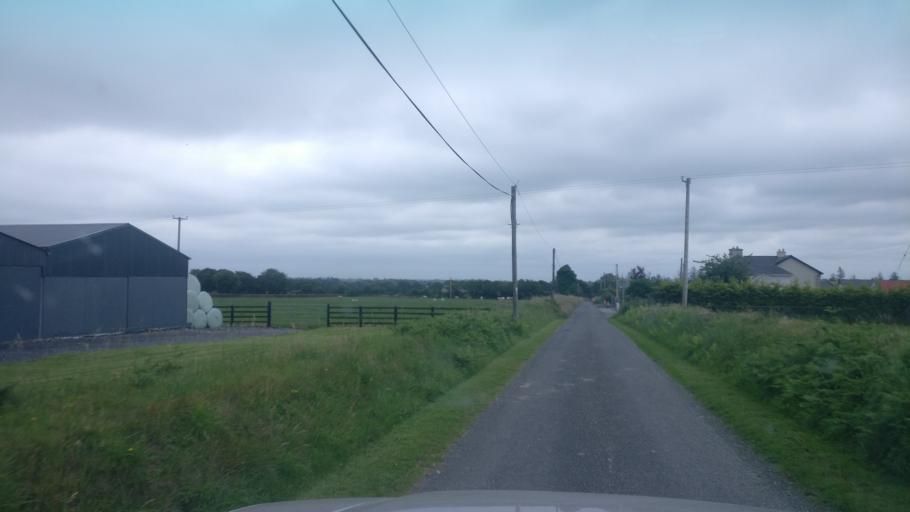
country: IE
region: Connaught
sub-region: County Galway
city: Ballinasloe
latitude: 53.3053
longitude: -8.3603
